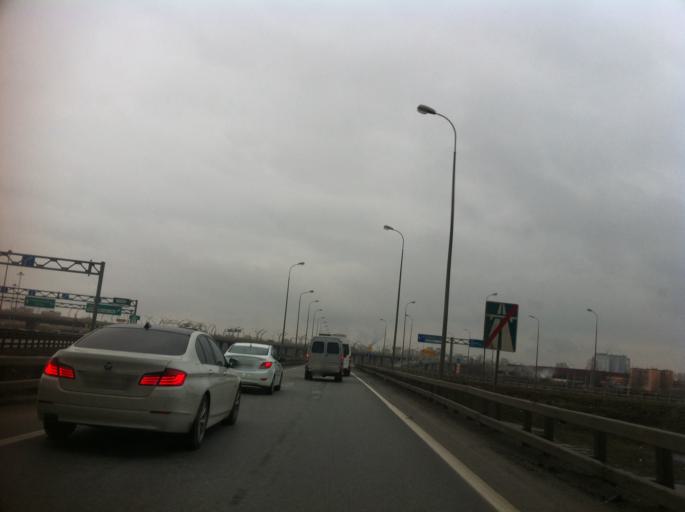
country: RU
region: St.-Petersburg
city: Dachnoye
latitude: 59.8320
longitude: 30.2854
